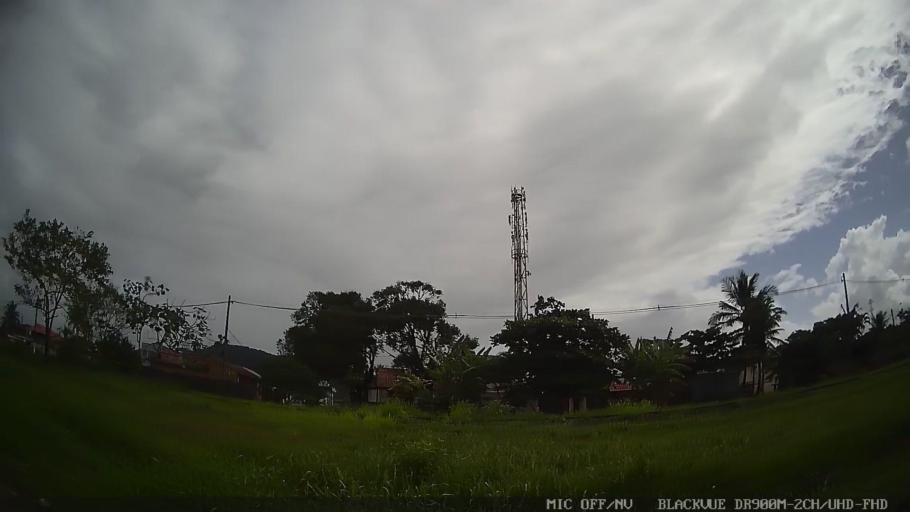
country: BR
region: Sao Paulo
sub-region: Itanhaem
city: Itanhaem
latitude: -24.1432
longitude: -46.7144
